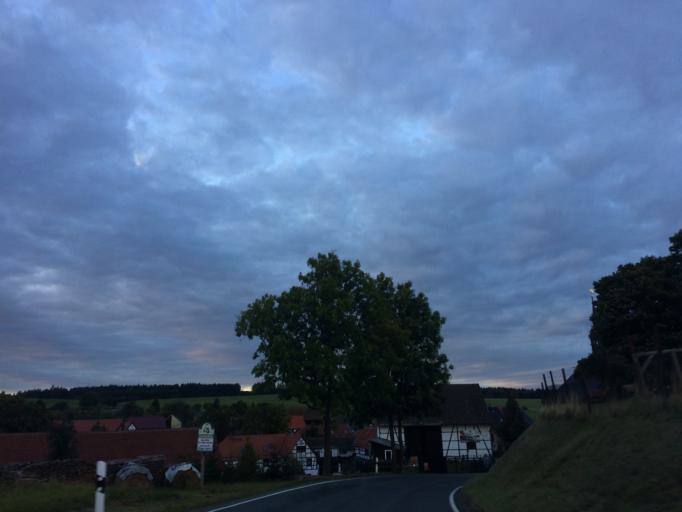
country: DE
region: Thuringia
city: Moxa
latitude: 50.6399
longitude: 11.6309
